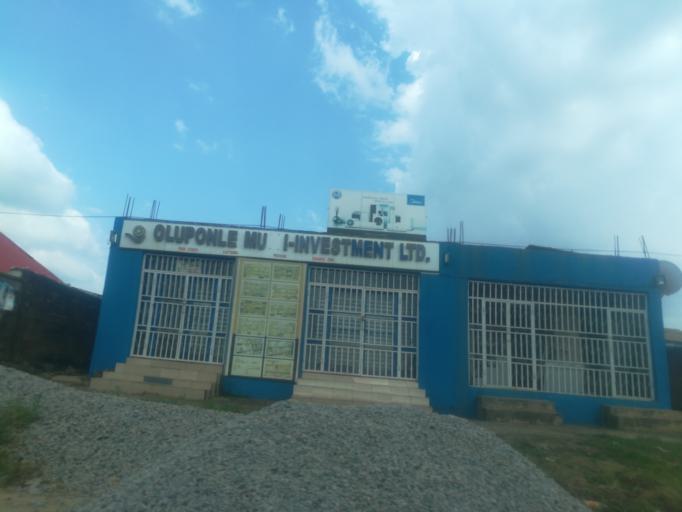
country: NG
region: Oyo
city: Ido
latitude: 7.4317
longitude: 3.8356
